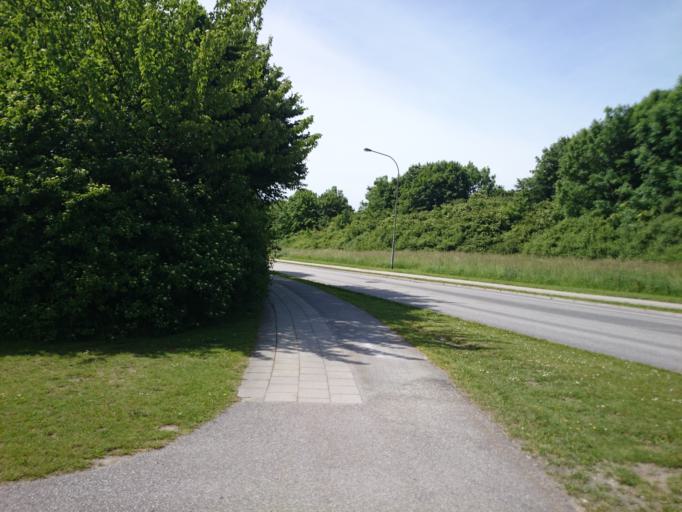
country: SE
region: Skane
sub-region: Lunds Kommun
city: Lund
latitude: 55.7135
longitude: 13.2228
